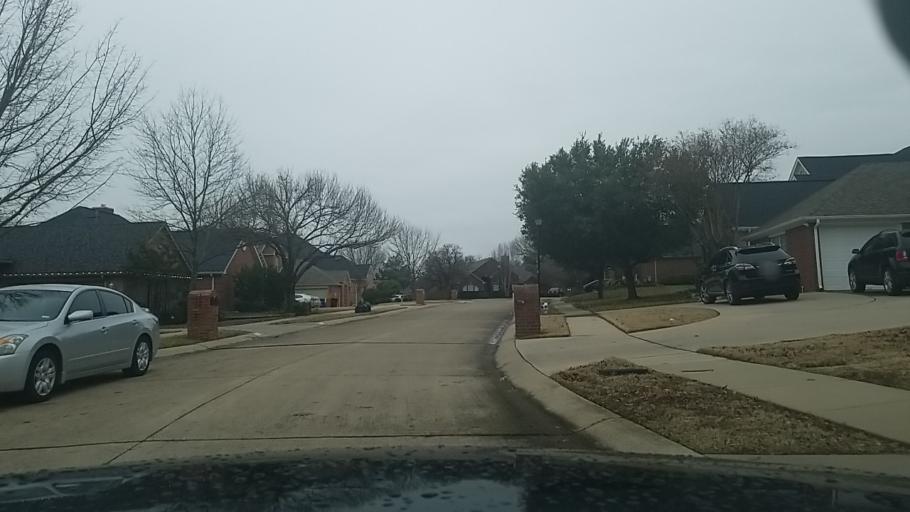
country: US
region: Texas
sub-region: Denton County
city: Corinth
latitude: 33.1578
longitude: -97.0795
